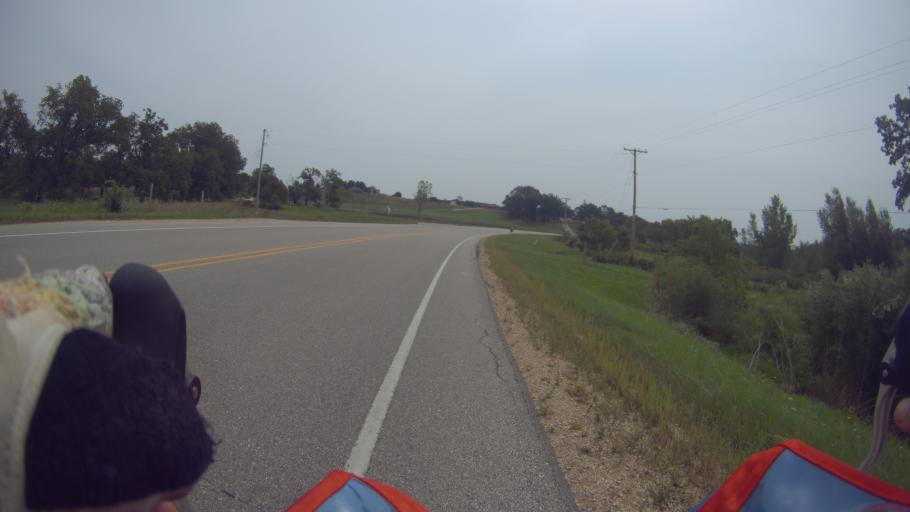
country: US
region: Wisconsin
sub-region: Dane County
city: Mount Horeb
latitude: 42.9625
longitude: -89.6741
